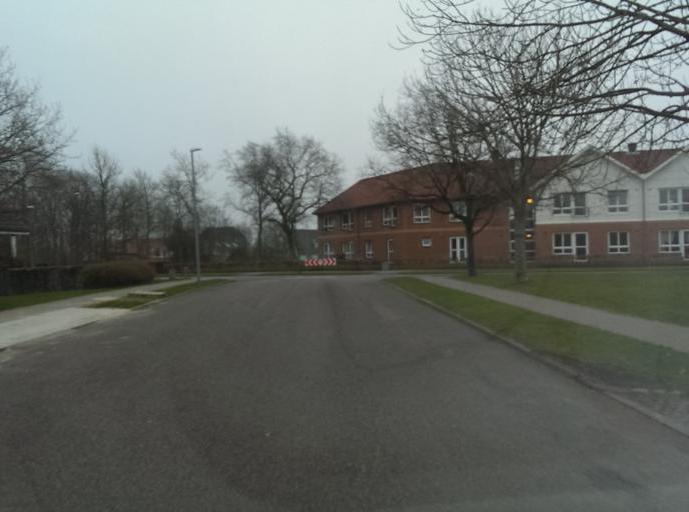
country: DK
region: South Denmark
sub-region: Esbjerg Kommune
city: Esbjerg
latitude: 55.4667
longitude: 8.4859
